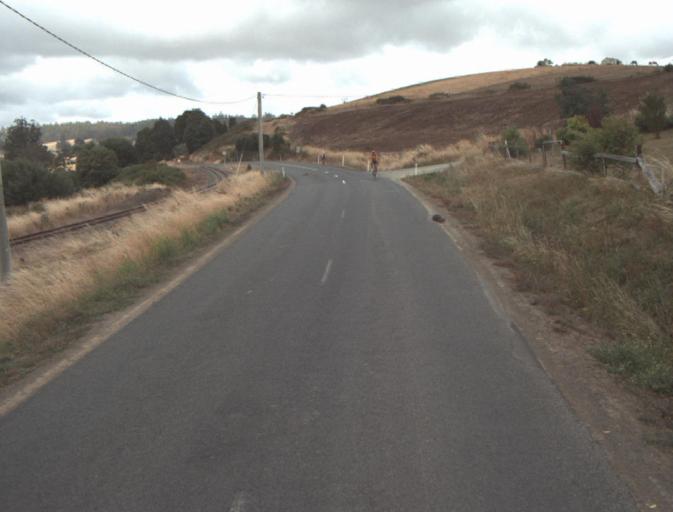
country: AU
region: Tasmania
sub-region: Launceston
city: Mayfield
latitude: -41.1815
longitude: 147.2233
